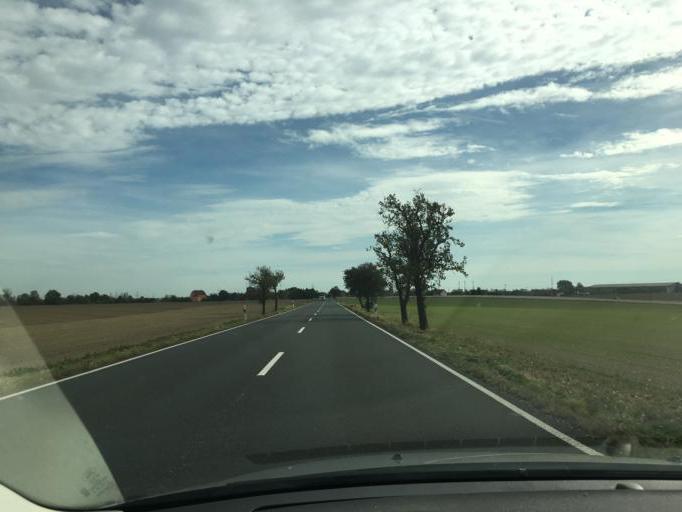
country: DE
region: Saxony
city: Lommatzsch
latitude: 51.2494
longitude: 13.2931
